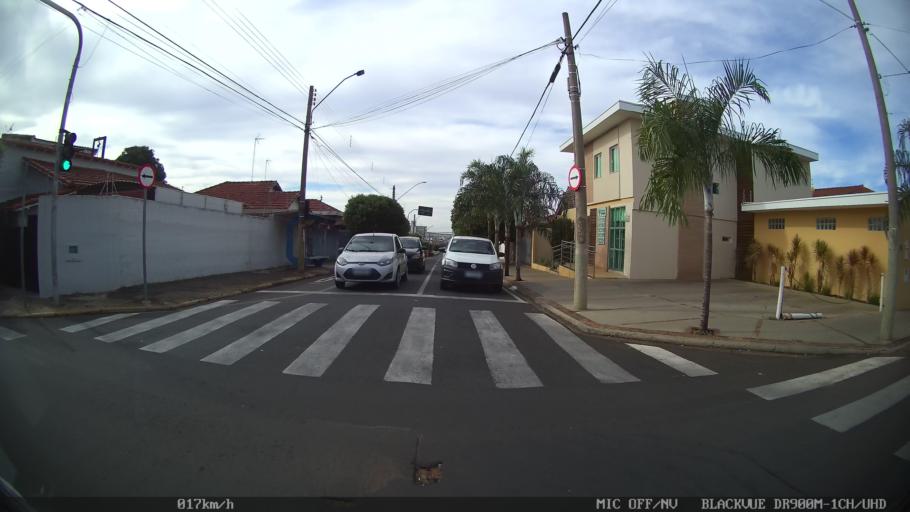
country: BR
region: Sao Paulo
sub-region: Catanduva
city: Catanduva
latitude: -21.1395
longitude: -48.9809
